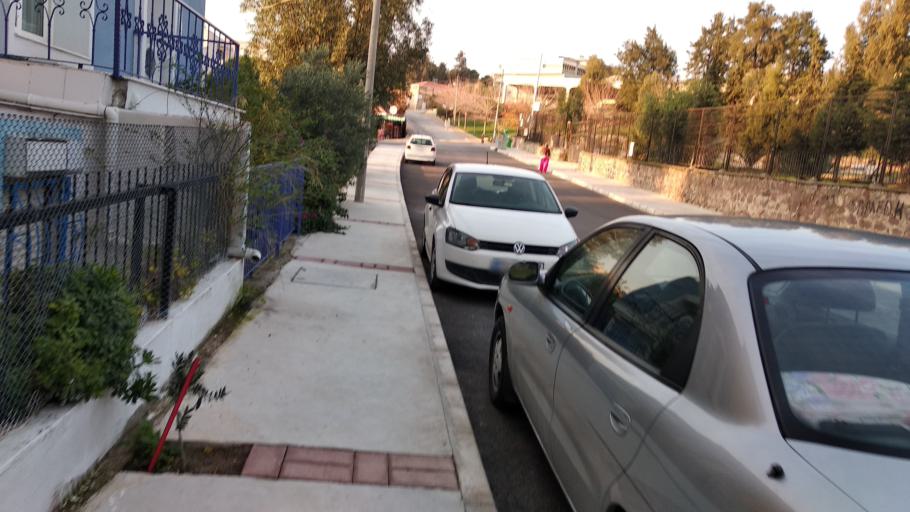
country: TR
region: Izmir
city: Karsiyaka
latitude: 38.4966
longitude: 27.0861
